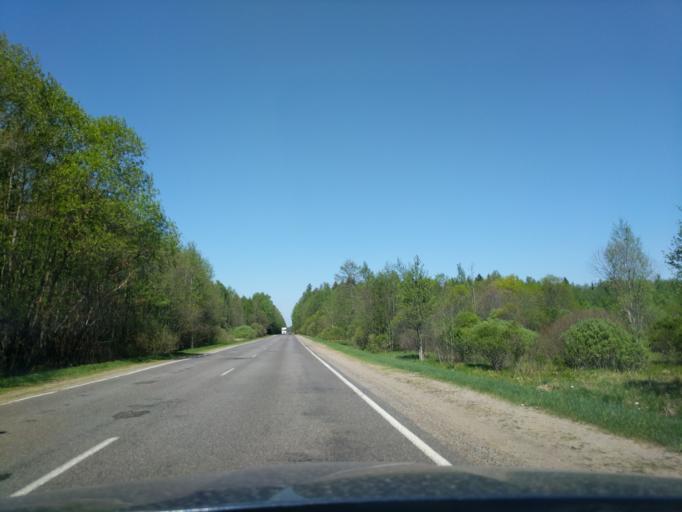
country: BY
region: Minsk
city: Il'ya
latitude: 54.4004
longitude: 27.3288
